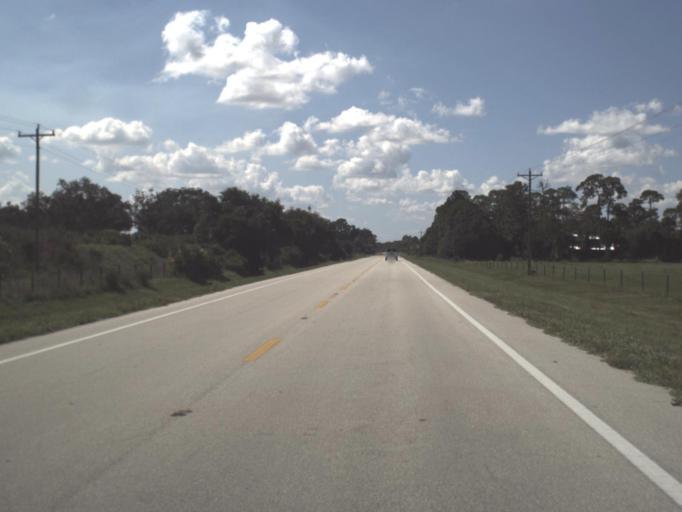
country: US
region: Florida
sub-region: Hendry County
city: Port LaBelle
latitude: 26.8160
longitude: -81.2920
